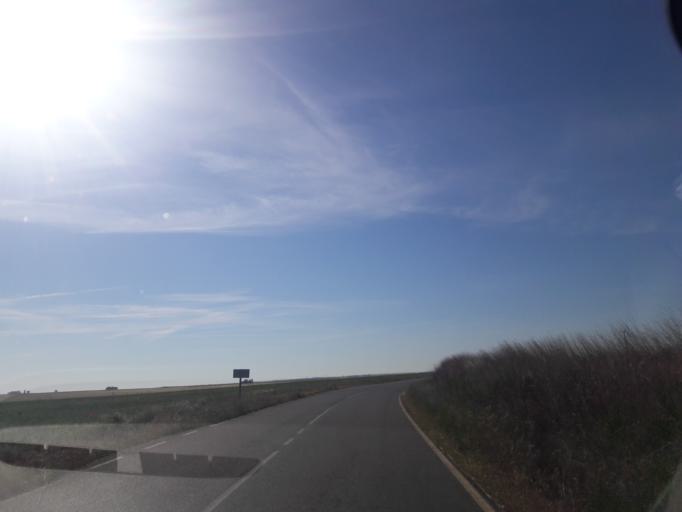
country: ES
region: Castille and Leon
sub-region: Provincia de Salamanca
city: Tardaguila
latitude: 41.1046
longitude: -5.5697
